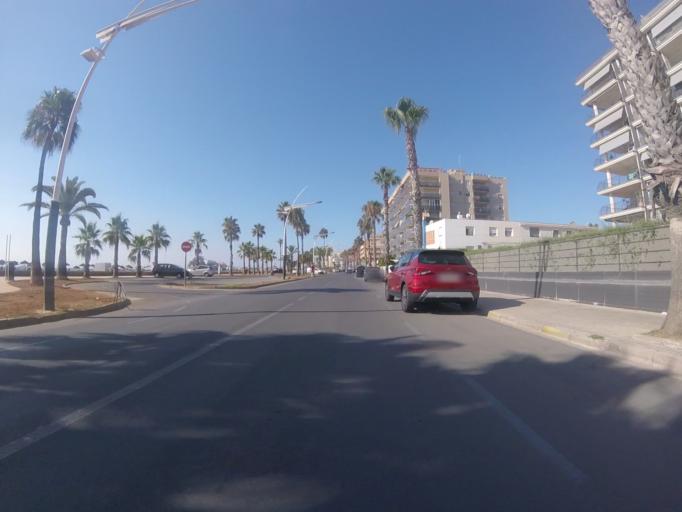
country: ES
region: Valencia
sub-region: Provincia de Castello
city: Peniscola
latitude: 40.3720
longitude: 0.4051
